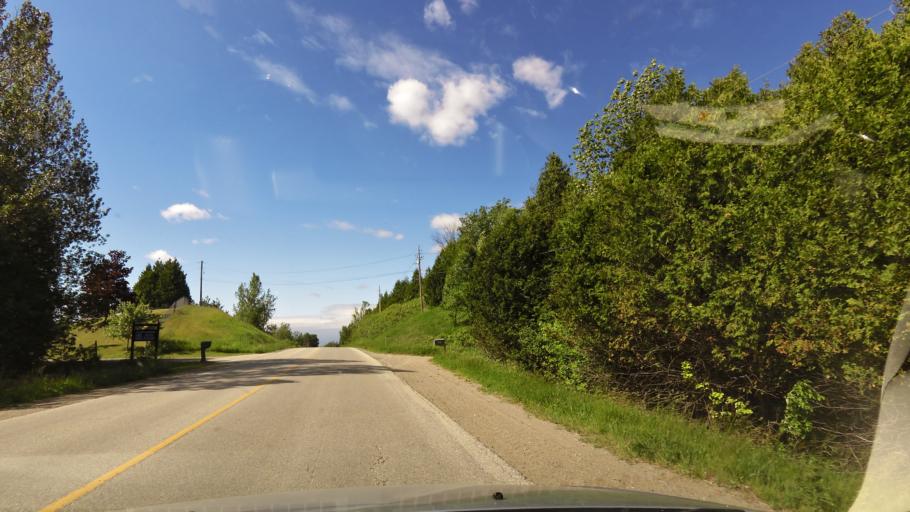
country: CA
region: Ontario
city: Bradford West Gwillimbury
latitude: 44.1745
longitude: -79.6186
